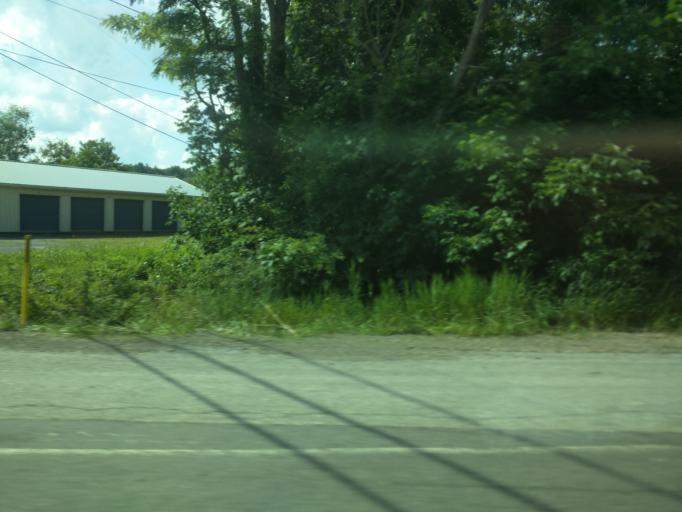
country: US
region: Pennsylvania
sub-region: Indiana County
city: Chevy Chase Heights
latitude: 40.7943
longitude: -79.1662
